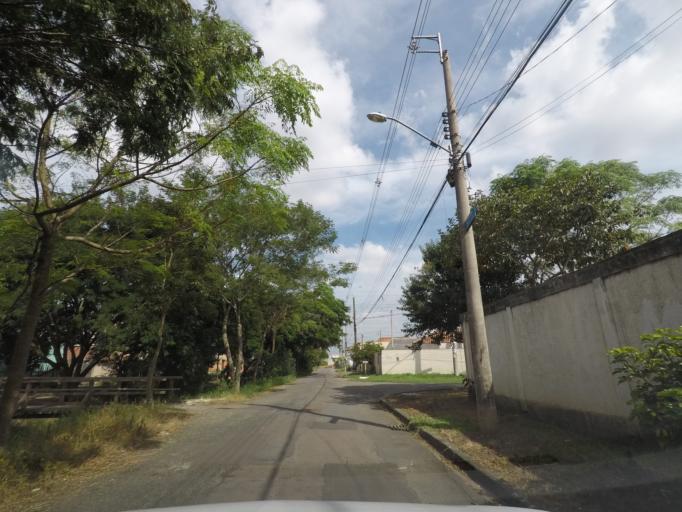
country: BR
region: Parana
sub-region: Pinhais
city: Pinhais
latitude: -25.4845
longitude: -49.1969
